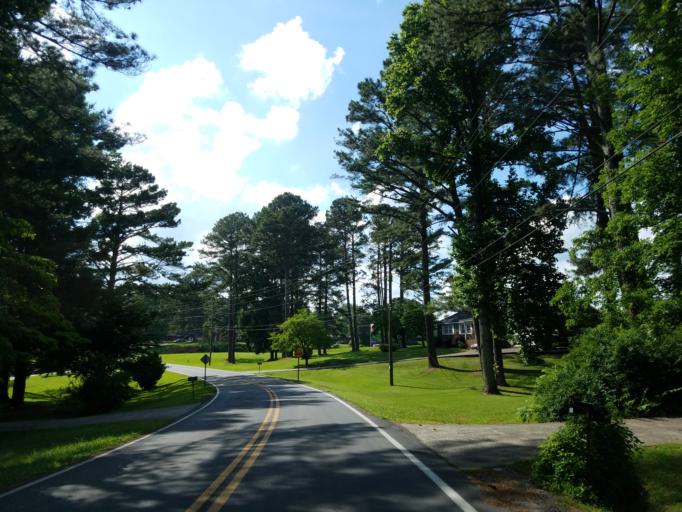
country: US
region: Georgia
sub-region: Pickens County
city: Jasper
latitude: 34.4710
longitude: -84.4210
